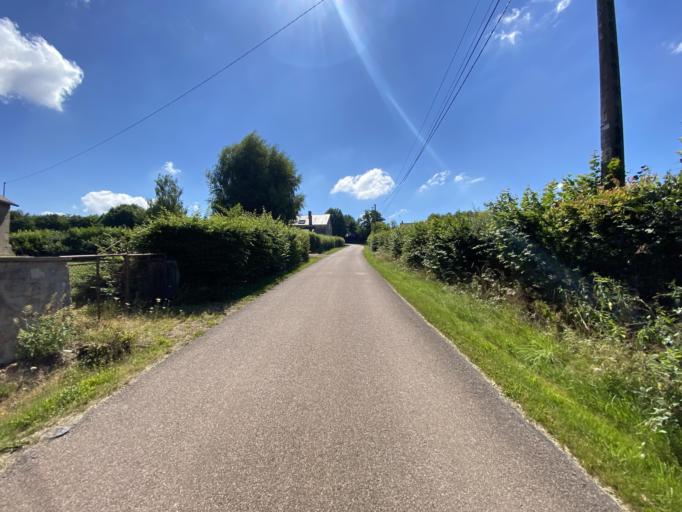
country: FR
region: Bourgogne
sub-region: Departement de la Cote-d'Or
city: Saulieu
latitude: 47.3238
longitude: 4.1521
